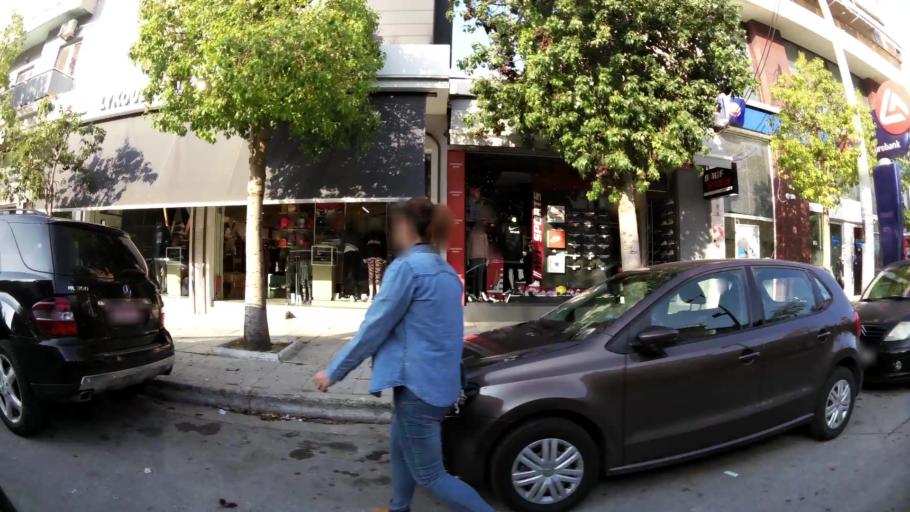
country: GR
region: Attica
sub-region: Nomarchia Athinas
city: Ilioupoli
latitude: 37.9331
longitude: 23.7561
